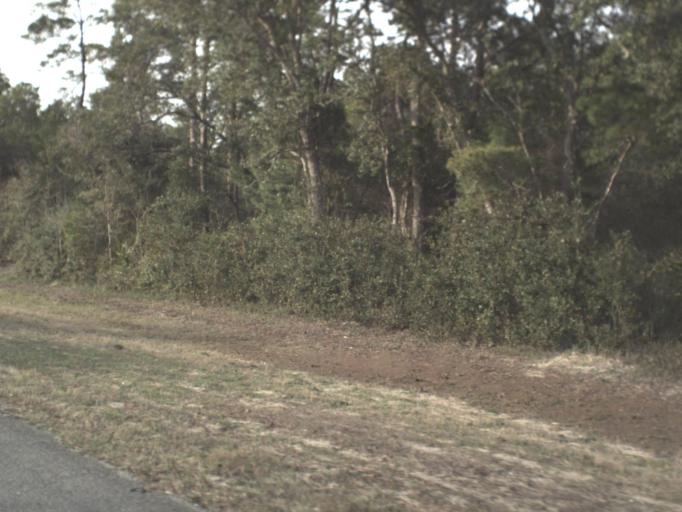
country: US
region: Florida
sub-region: Bay County
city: Mexico Beach
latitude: 29.9634
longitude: -85.4443
